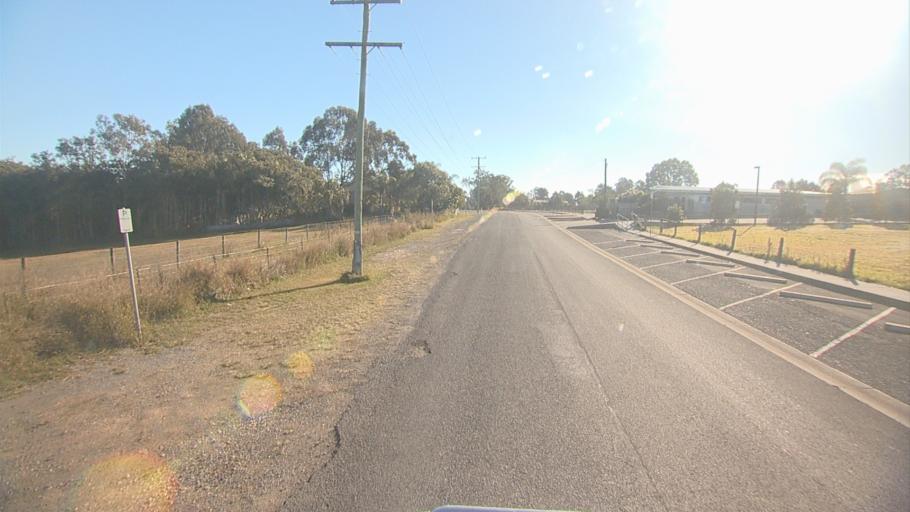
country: AU
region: Queensland
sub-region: Logan
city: Chambers Flat
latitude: -27.7646
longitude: 153.1049
